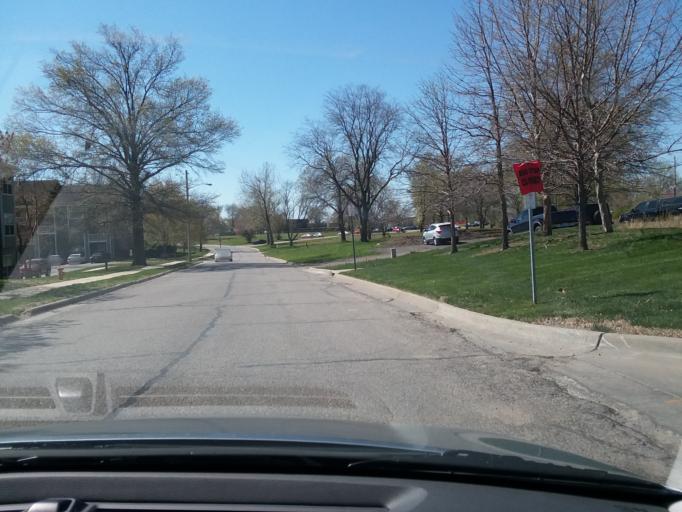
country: US
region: Kansas
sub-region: Douglas County
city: Lawrence
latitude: 38.9489
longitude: -95.2592
